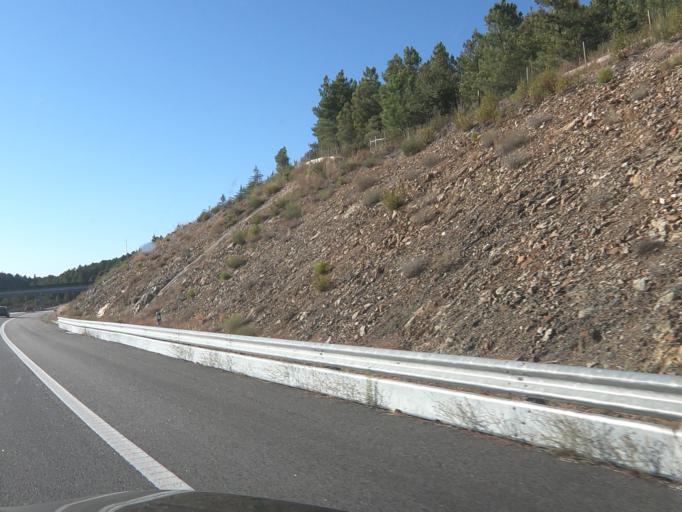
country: PT
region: Vila Real
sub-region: Murca
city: Murca
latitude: 41.4255
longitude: -7.3881
